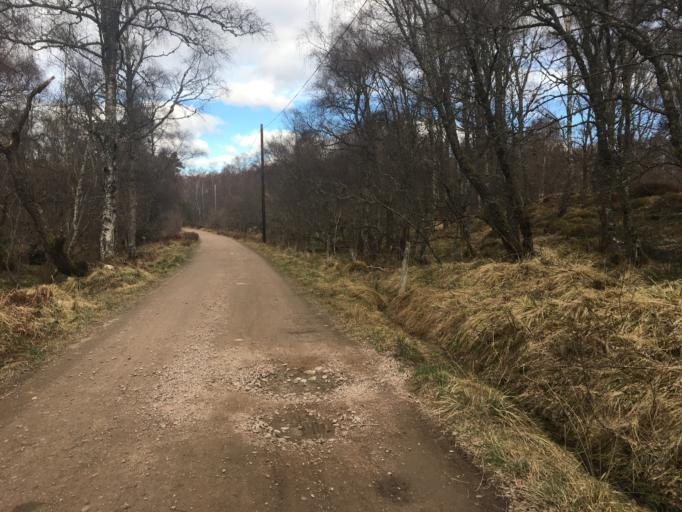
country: GB
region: Scotland
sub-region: Highland
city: Aviemore
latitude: 57.1641
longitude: -3.8127
